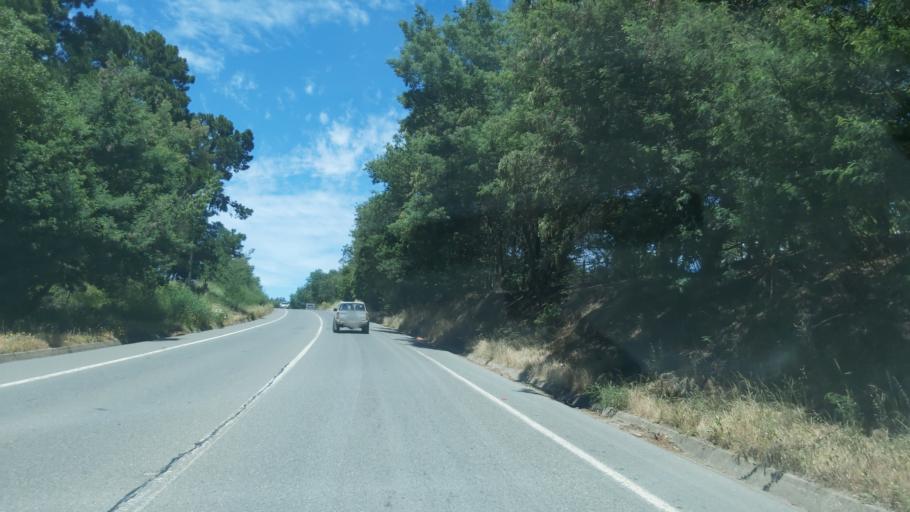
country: CL
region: Maule
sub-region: Provincia de Talca
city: Constitucion
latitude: -35.3255
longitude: -72.3856
